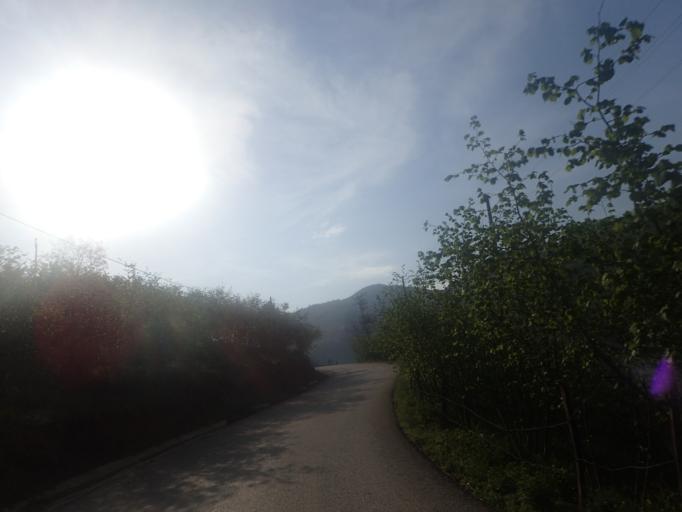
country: TR
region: Ordu
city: Catalpinar
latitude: 40.8792
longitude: 37.4761
